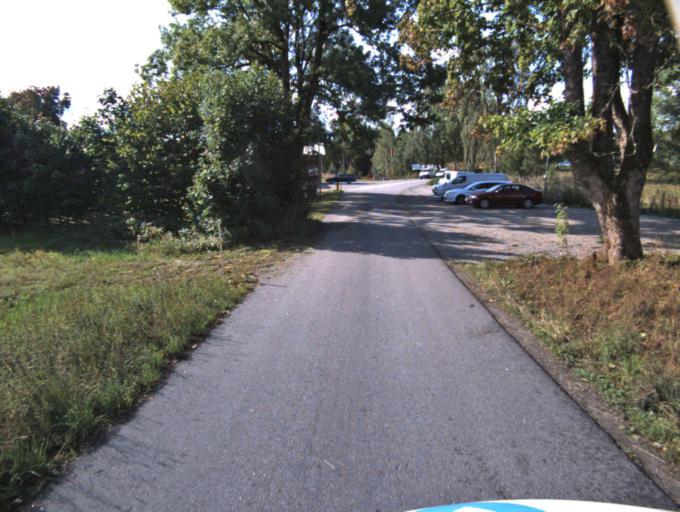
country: SE
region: Vaestra Goetaland
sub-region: Ulricehamns Kommun
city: Ulricehamn
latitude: 57.6758
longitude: 13.4720
